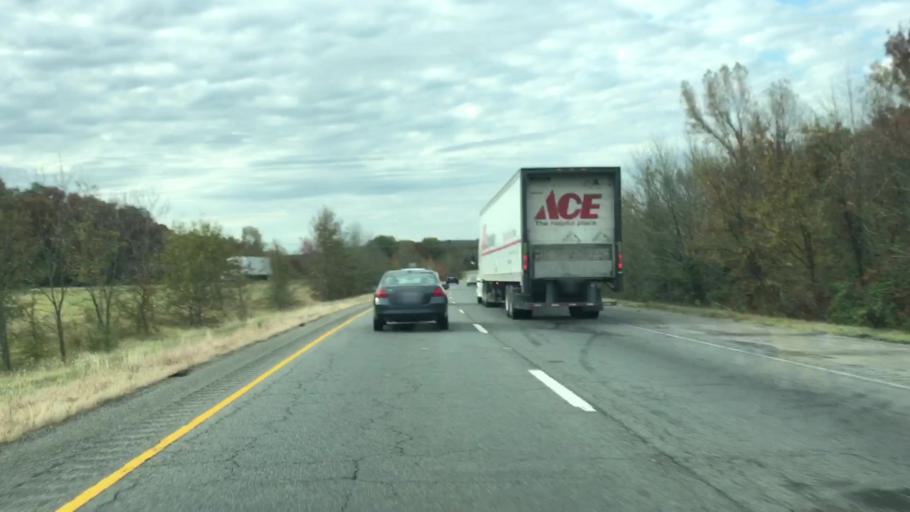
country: US
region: Arkansas
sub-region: Faulkner County
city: Conway
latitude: 35.1243
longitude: -92.5069
